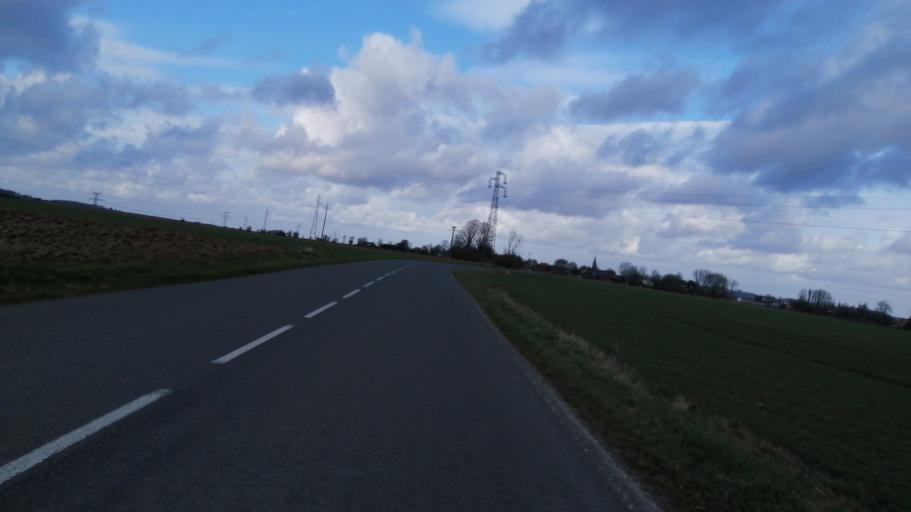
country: FR
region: Nord-Pas-de-Calais
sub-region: Departement du Pas-de-Calais
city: Beaurains
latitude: 50.2402
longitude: 2.8068
